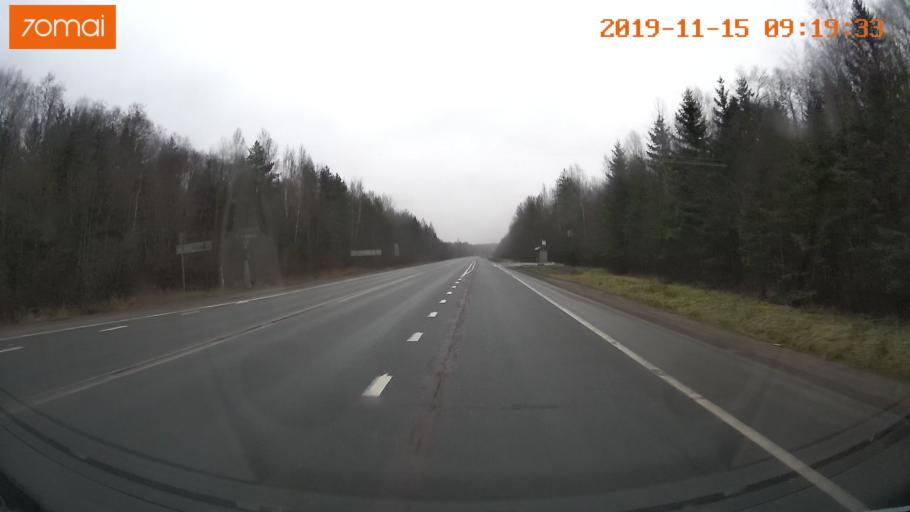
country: RU
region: Vologda
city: Tonshalovo
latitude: 59.2846
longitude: 38.0181
